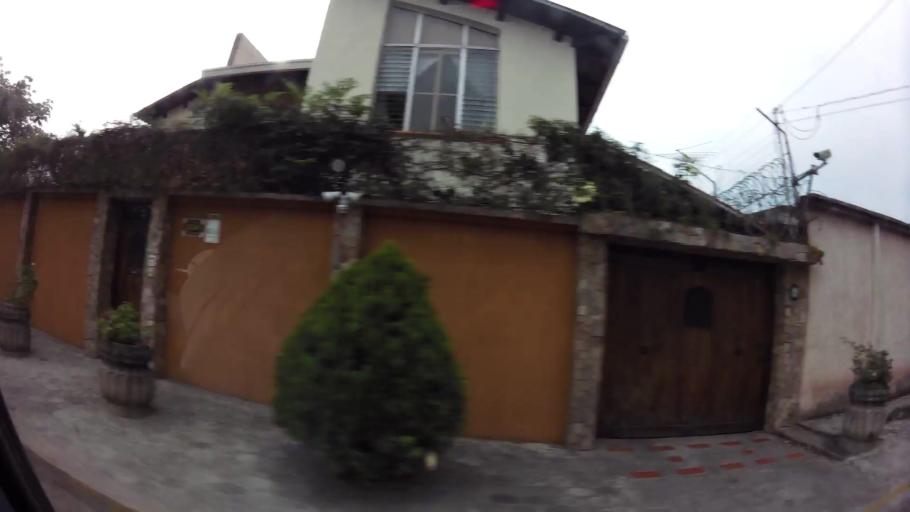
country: HN
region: Francisco Morazan
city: Tegucigalpa
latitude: 14.0800
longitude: -87.2018
